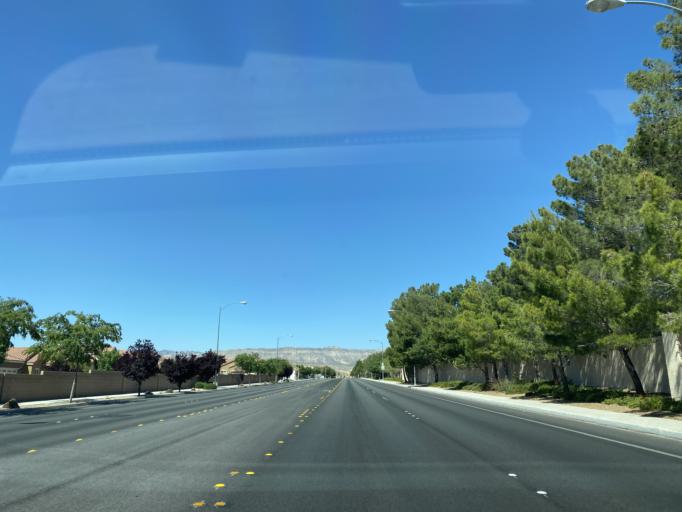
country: US
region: Nevada
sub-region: Clark County
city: Spring Valley
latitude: 36.0923
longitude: -115.2635
